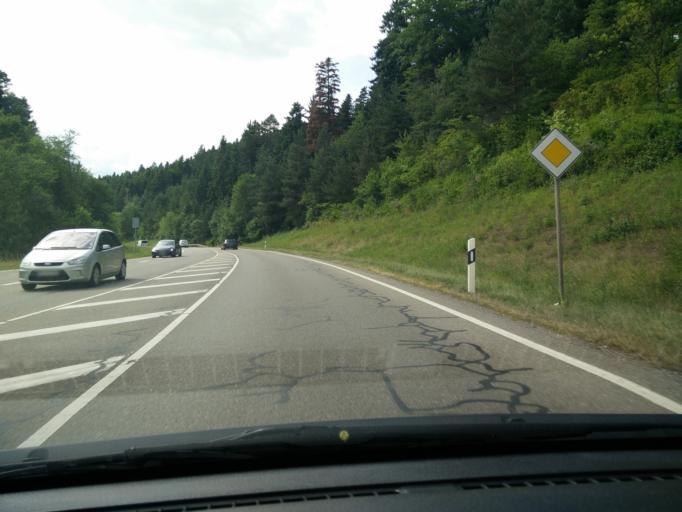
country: DE
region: Baden-Wuerttemberg
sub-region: Freiburg Region
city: Deisslingen
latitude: 48.0832
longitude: 8.6093
